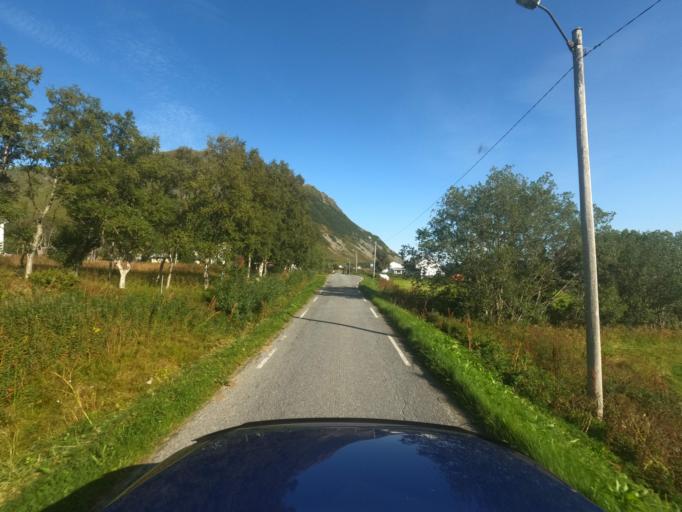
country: NO
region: Nordland
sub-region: Vestvagoy
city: Evjen
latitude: 68.2929
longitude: 14.0013
